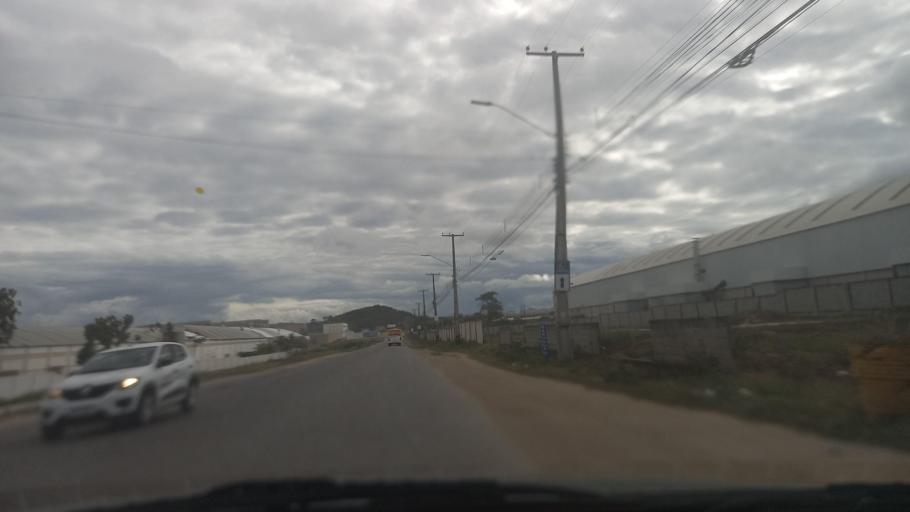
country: BR
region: Pernambuco
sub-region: Caruaru
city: Caruaru
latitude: -8.2890
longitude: -36.0129
